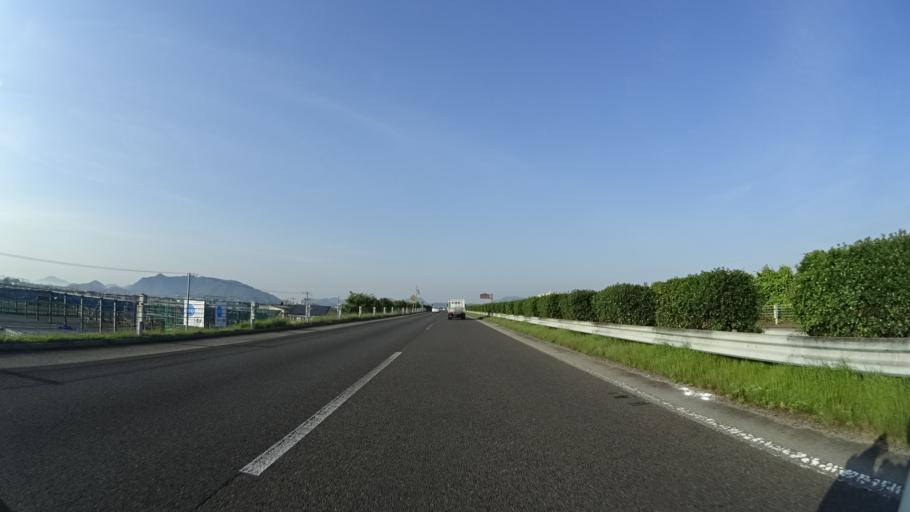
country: JP
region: Kagawa
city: Kan'onjicho
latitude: 34.0886
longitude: 133.6584
